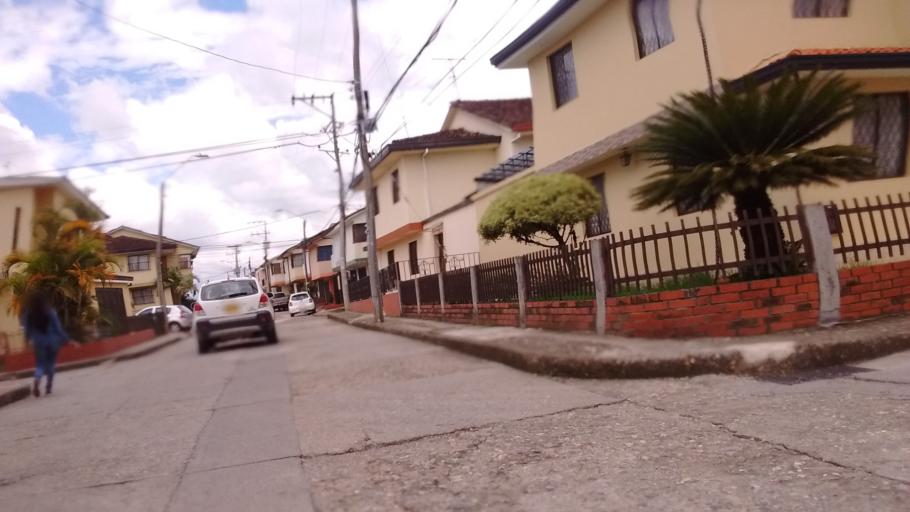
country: CO
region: Cauca
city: Popayan
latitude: 2.4610
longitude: -76.5873
